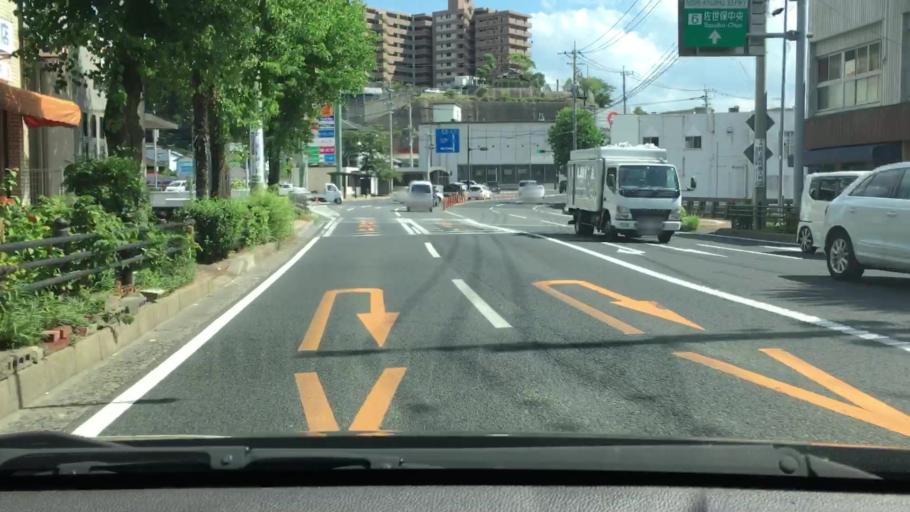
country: JP
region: Nagasaki
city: Sasebo
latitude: 33.2070
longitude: 129.7209
